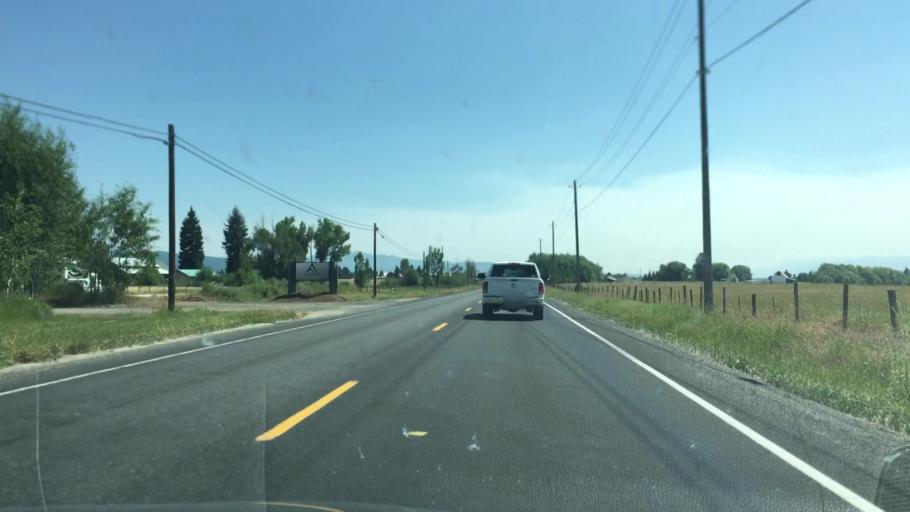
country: US
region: Idaho
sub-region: Valley County
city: McCall
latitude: 44.8464
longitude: -116.0893
